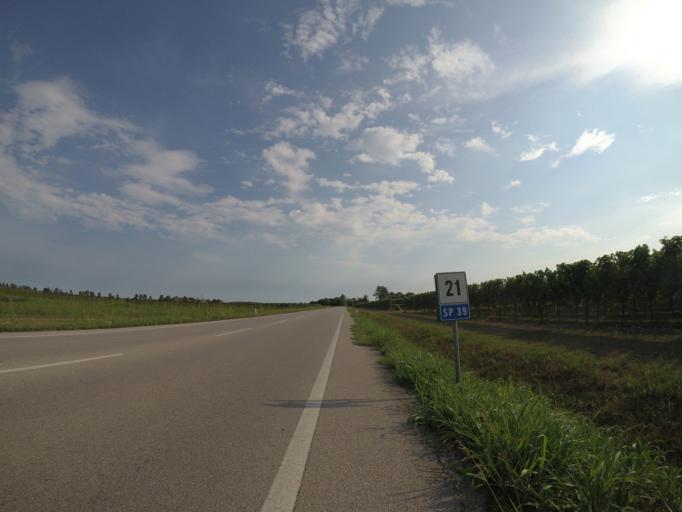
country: IT
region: Friuli Venezia Giulia
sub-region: Provincia di Udine
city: Codroipo
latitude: 45.9388
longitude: 12.9782
